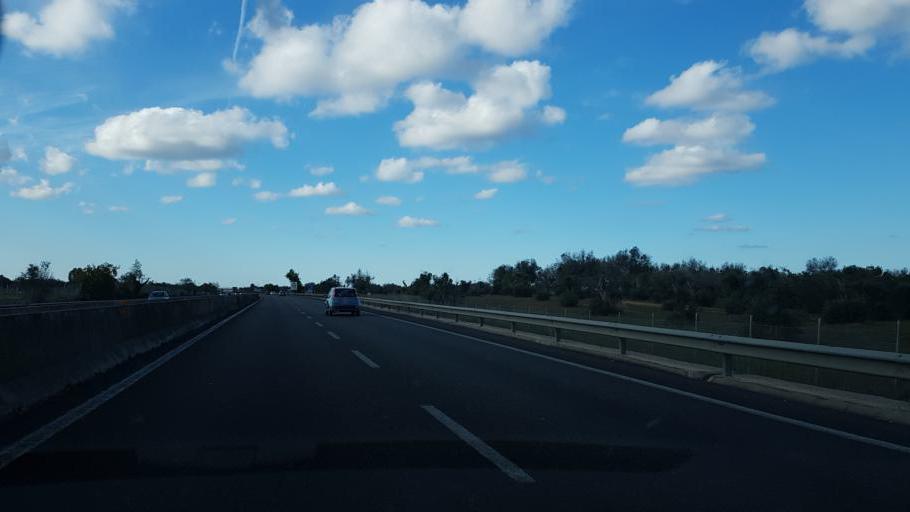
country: IT
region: Apulia
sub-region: Provincia di Lecce
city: Trepuzzi
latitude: 40.4156
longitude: 18.1006
